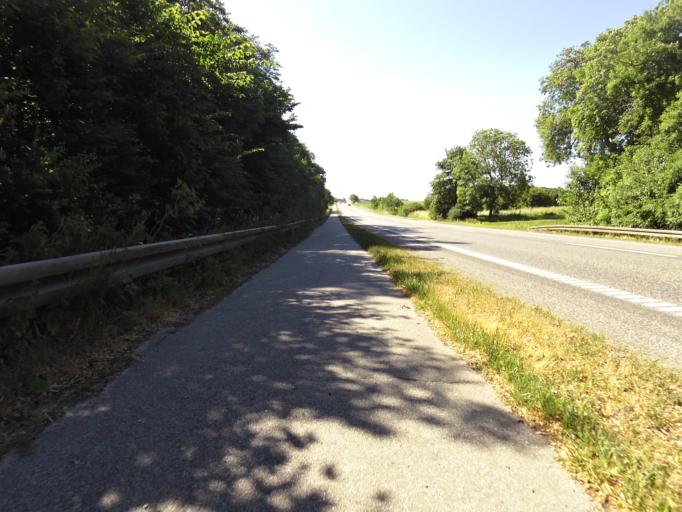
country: DK
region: Central Jutland
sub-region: Struer Kommune
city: Struer
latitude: 56.4590
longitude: 8.5905
